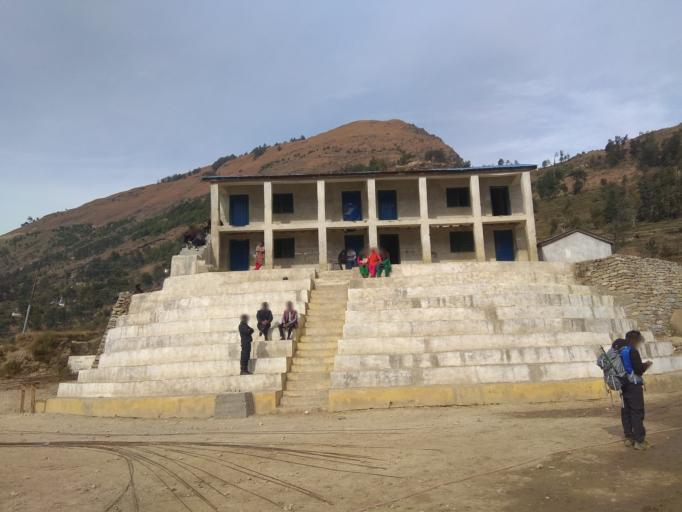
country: NP
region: Mid Western
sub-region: Bheri Zone
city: Dailekh
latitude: 29.2434
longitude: 81.6625
